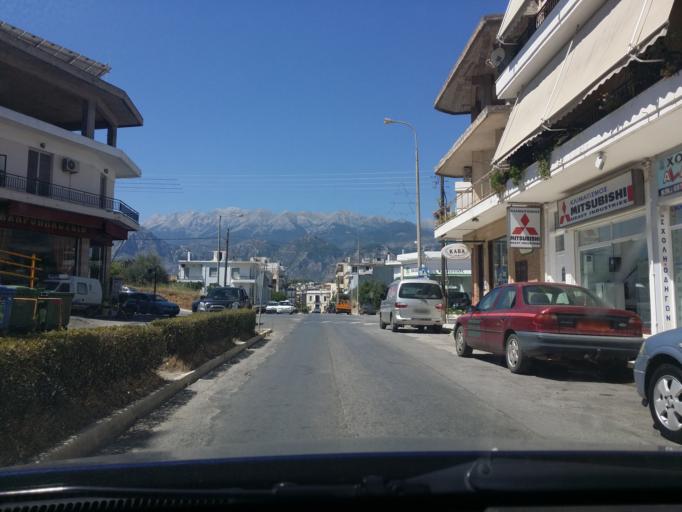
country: GR
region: Peloponnese
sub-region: Nomos Lakonias
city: Sparti
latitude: 37.0786
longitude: 22.4312
